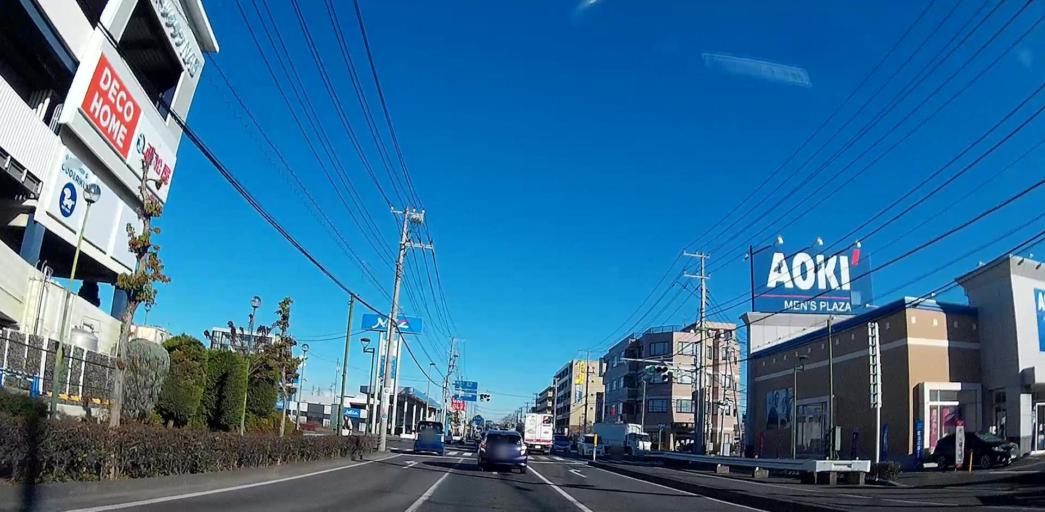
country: JP
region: Chiba
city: Shiroi
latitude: 35.7813
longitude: 140.0023
